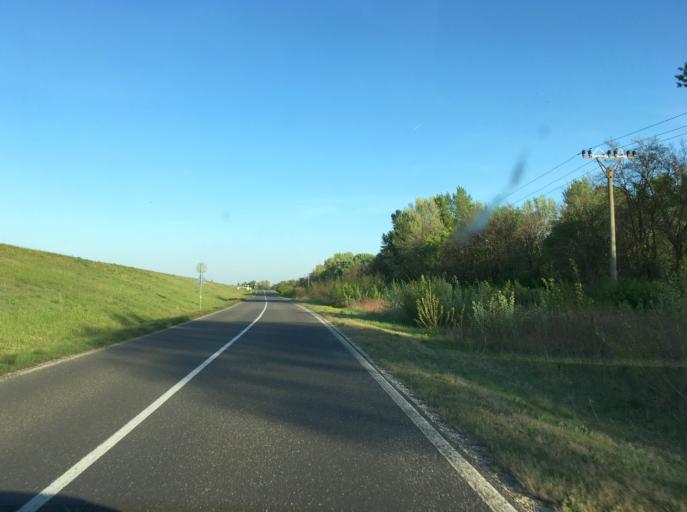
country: SK
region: Trnavsky
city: Samorin
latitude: 48.0023
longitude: 17.2573
